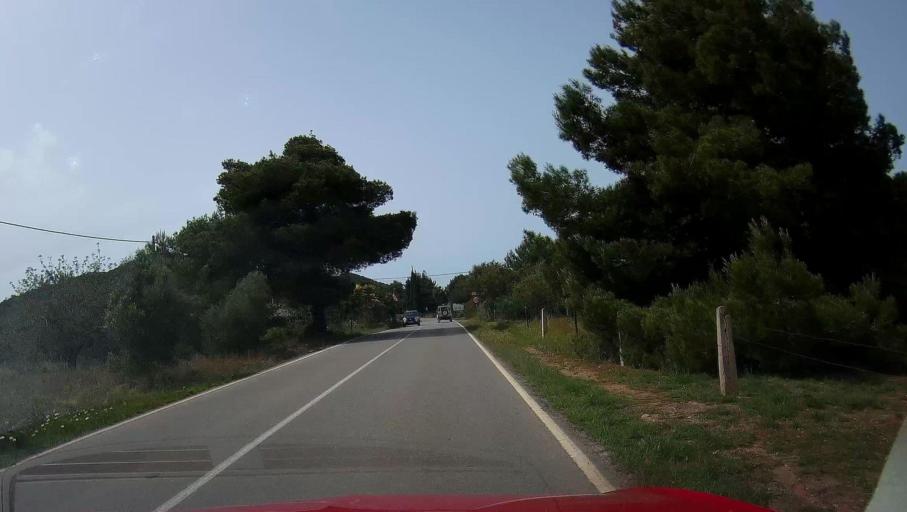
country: ES
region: Balearic Islands
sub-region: Illes Balears
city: Santa Eularia des Riu
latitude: 38.9896
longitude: 1.4876
